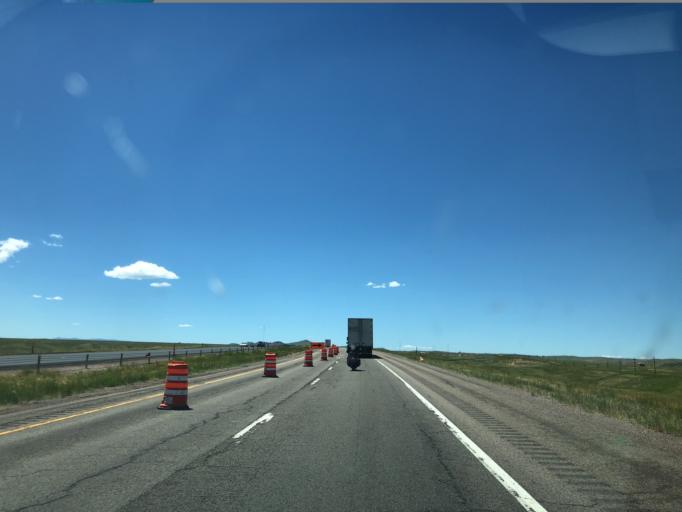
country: US
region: Wyoming
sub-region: Laramie County
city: Cheyenne
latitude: 41.0993
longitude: -105.0947
